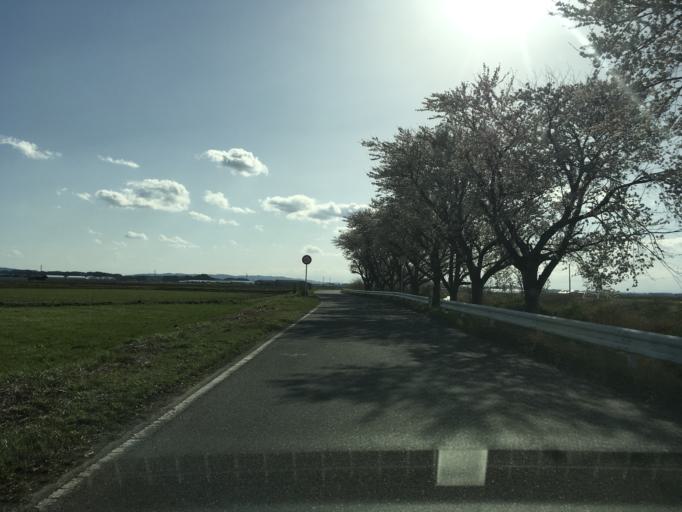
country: JP
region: Miyagi
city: Wakuya
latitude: 38.6650
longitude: 141.2495
